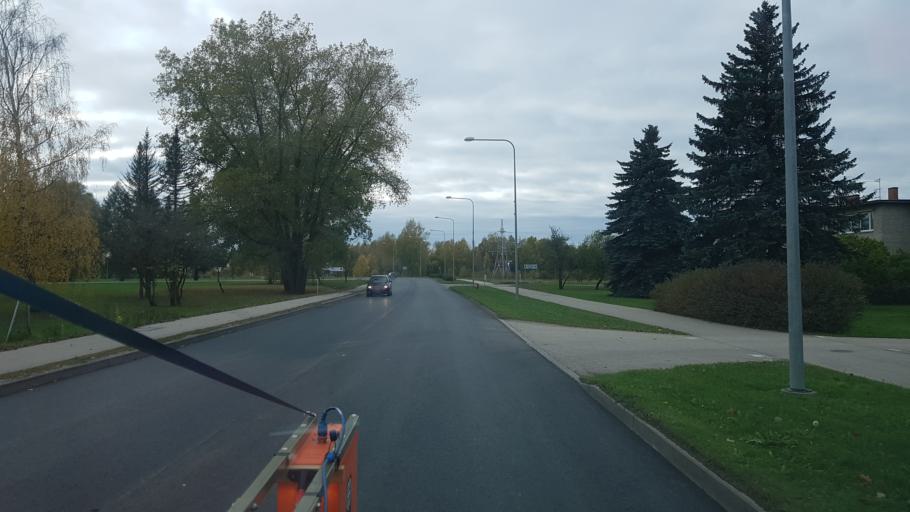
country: EE
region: Polvamaa
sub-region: Polva linn
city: Polva
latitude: 58.0698
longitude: 27.0799
